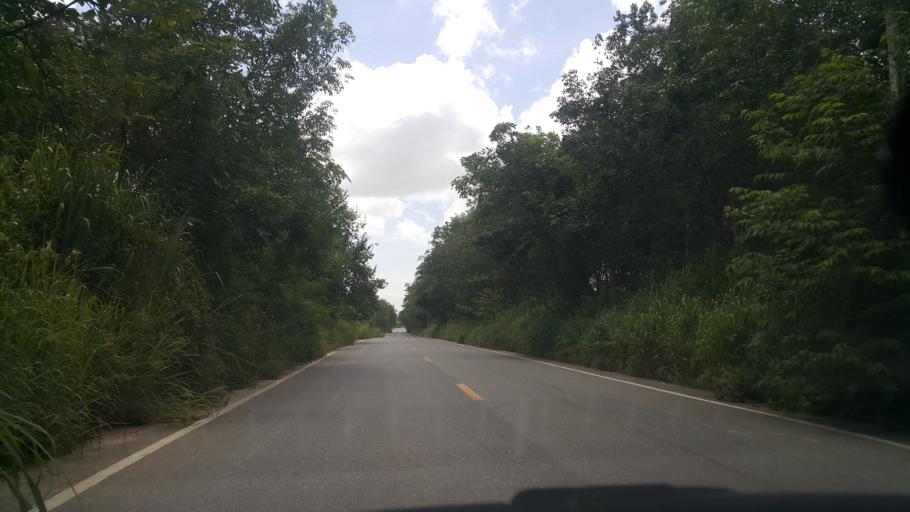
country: TH
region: Rayong
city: Ban Chang
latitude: 12.8011
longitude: 101.0196
